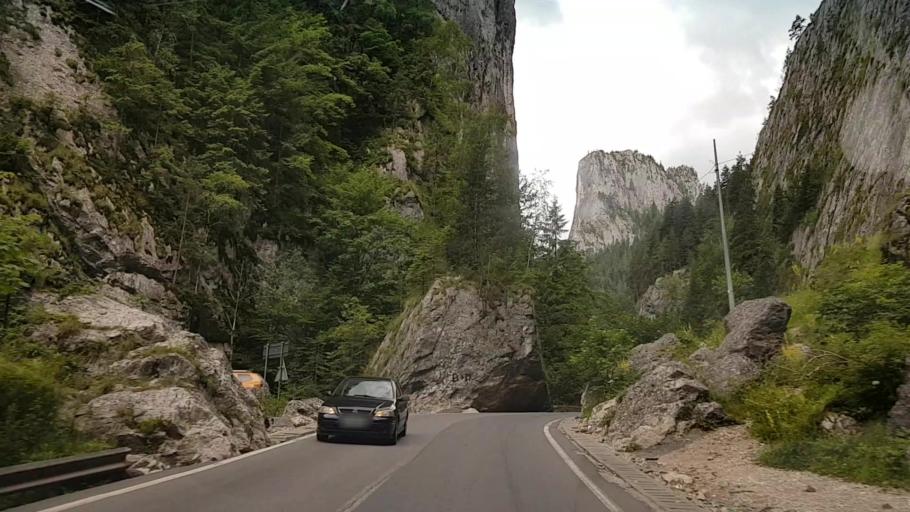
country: RO
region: Neamt
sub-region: Comuna Bicaz Chei
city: Bicaz Chei
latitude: 46.8112
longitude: 25.8252
